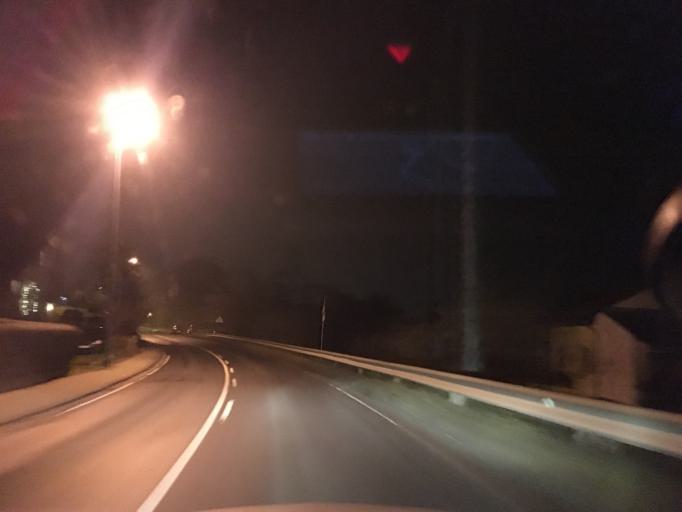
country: DE
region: Hesse
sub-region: Regierungsbezirk Darmstadt
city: Hofheim am Taunus
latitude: 50.0634
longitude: 8.4243
